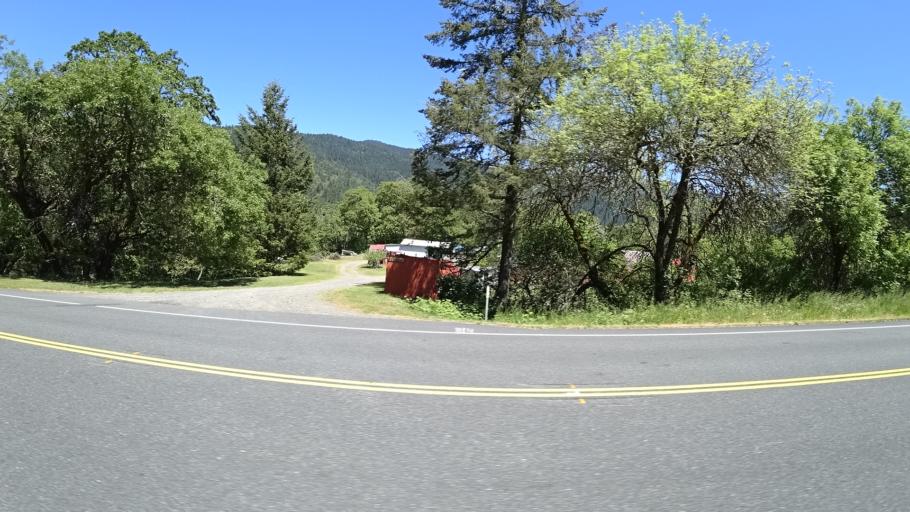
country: US
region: California
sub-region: Humboldt County
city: Willow Creek
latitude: 40.8805
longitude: -123.5419
